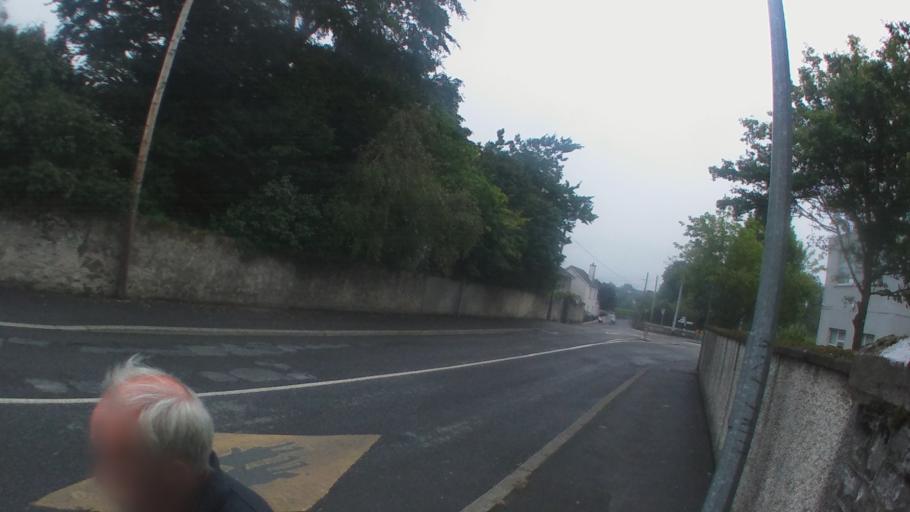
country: IE
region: Leinster
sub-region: Kilkenny
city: Callan
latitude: 52.5477
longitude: -7.3881
